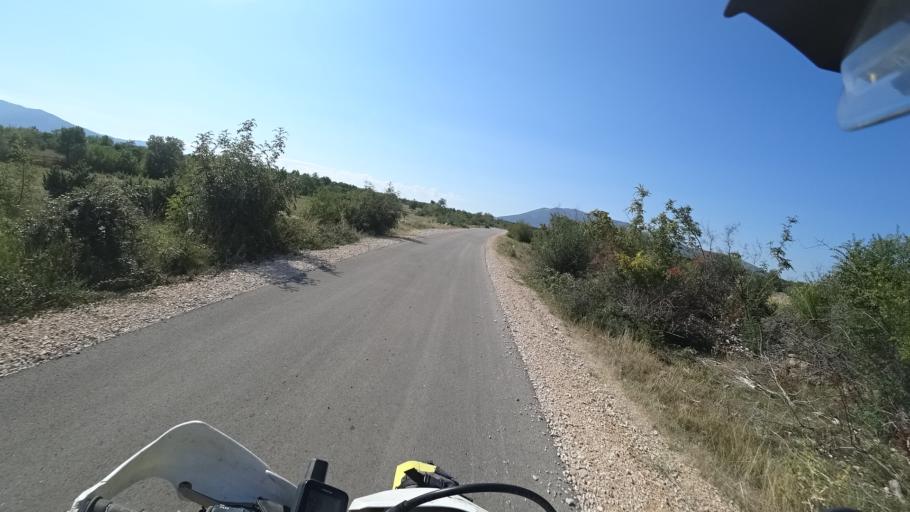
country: HR
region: Sibensko-Kniniska
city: Knin
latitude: 44.0061
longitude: 16.1934
